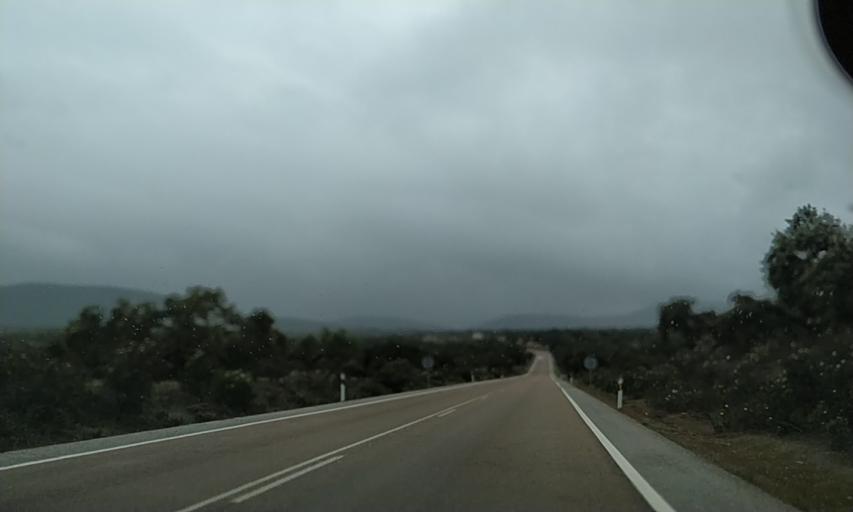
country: ES
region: Extremadura
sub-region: Provincia de Badajoz
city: Puebla de Obando
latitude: 39.2187
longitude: -6.5790
